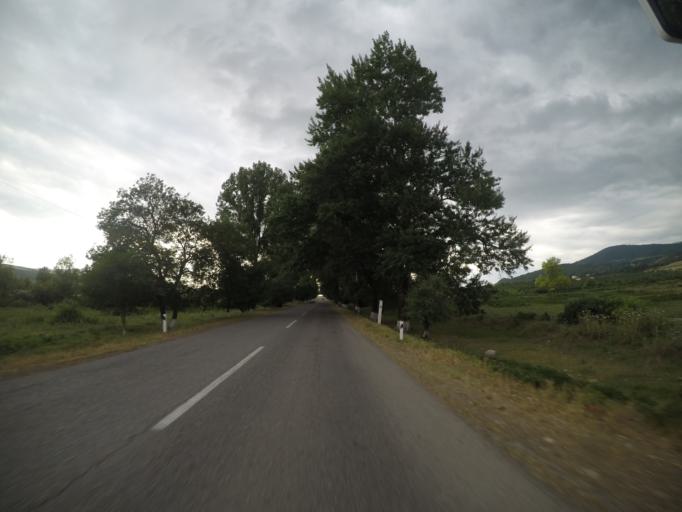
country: AZ
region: Ismayilli
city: Ismayilli
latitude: 40.7526
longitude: 48.2348
